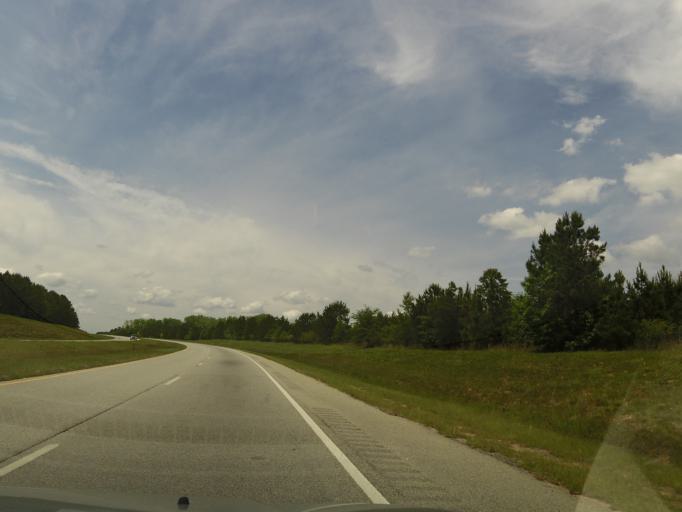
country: US
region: Georgia
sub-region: Emanuel County
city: Swainsboro
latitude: 32.5654
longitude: -82.3439
